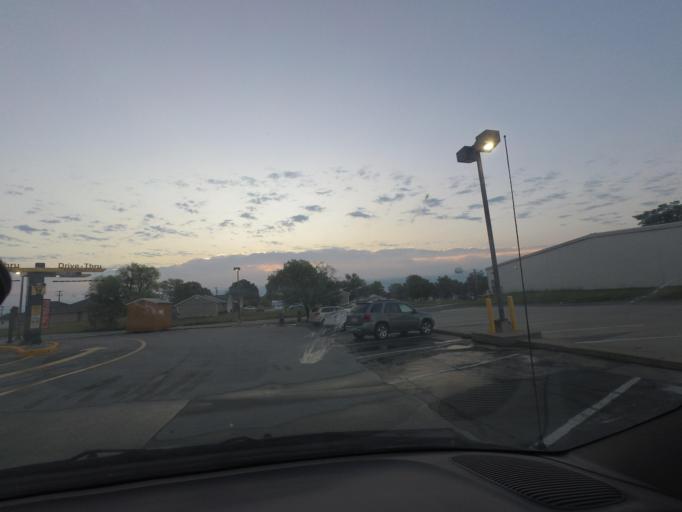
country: US
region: Missouri
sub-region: Macon County
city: Macon
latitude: 39.7501
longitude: -92.4673
